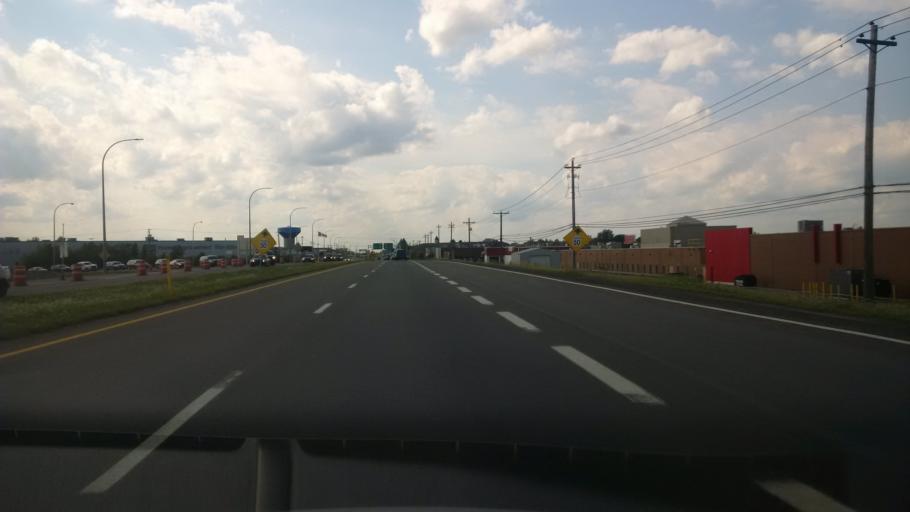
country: CA
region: New Brunswick
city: Fredericton
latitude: 45.9378
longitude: -66.6624
